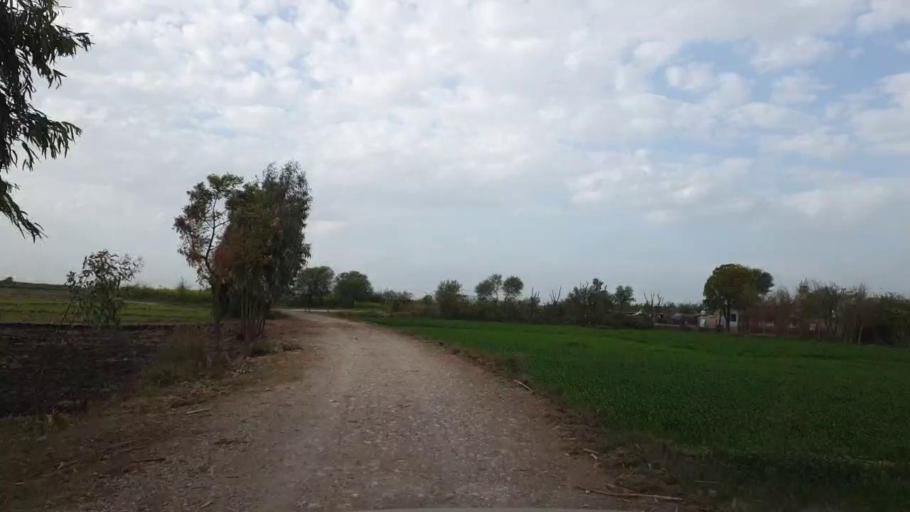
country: PK
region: Sindh
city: Tando Adam
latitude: 25.6584
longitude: 68.6108
